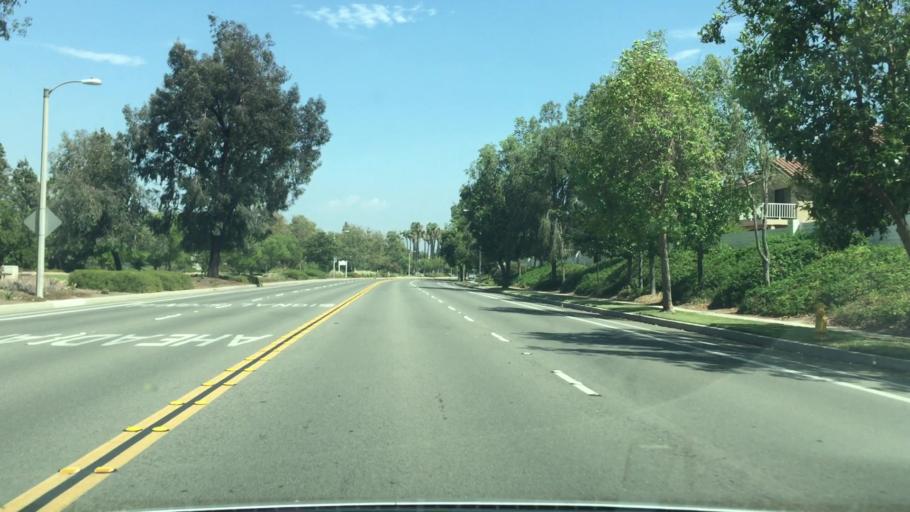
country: US
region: California
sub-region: San Bernardino County
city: Los Serranos
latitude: 33.9334
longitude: -117.6701
